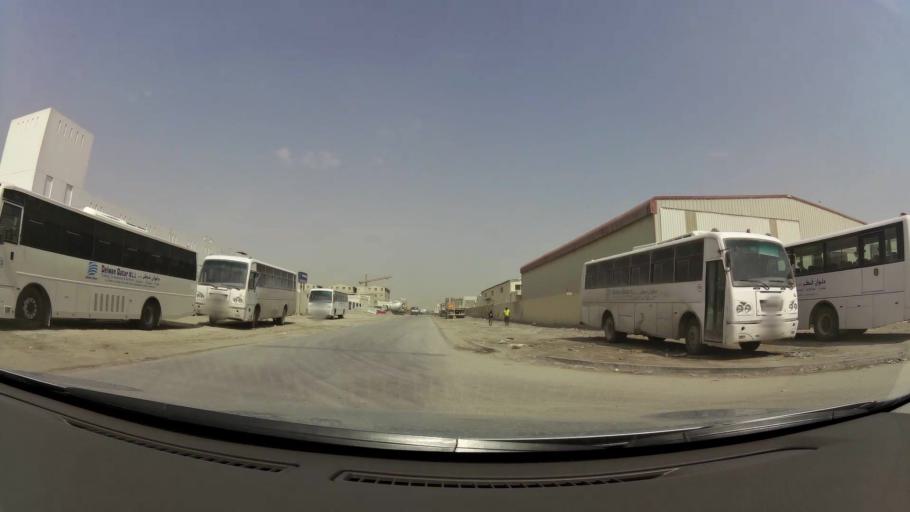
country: QA
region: Al Wakrah
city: Al Wukayr
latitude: 25.1681
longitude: 51.4404
